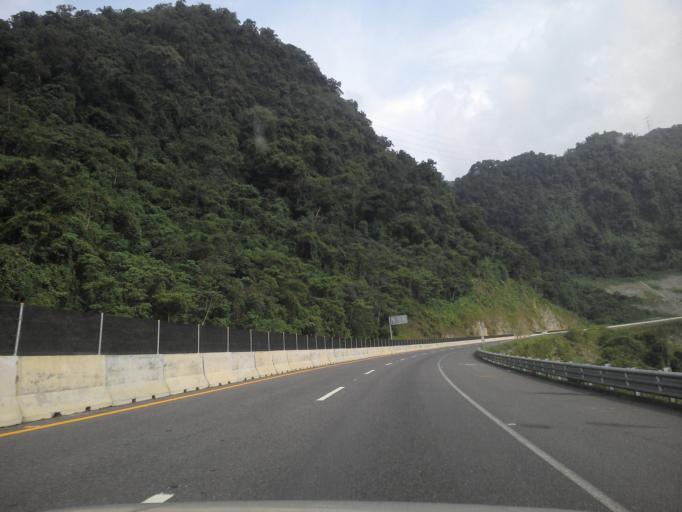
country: MX
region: Puebla
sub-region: Xicotepec
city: San Lorenzo
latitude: 20.3371
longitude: -97.9586
